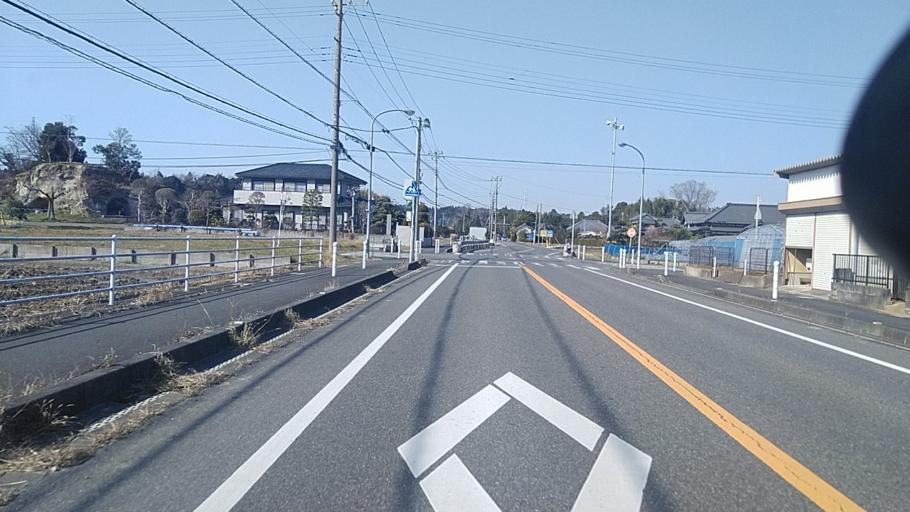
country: JP
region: Chiba
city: Mobara
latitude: 35.4585
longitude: 140.2867
